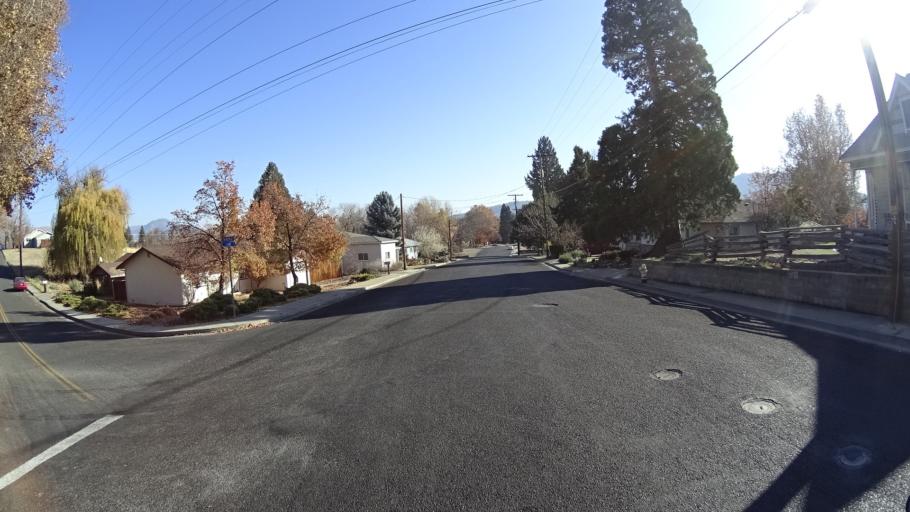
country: US
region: California
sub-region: Siskiyou County
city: Yreka
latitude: 41.7317
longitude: -122.6466
